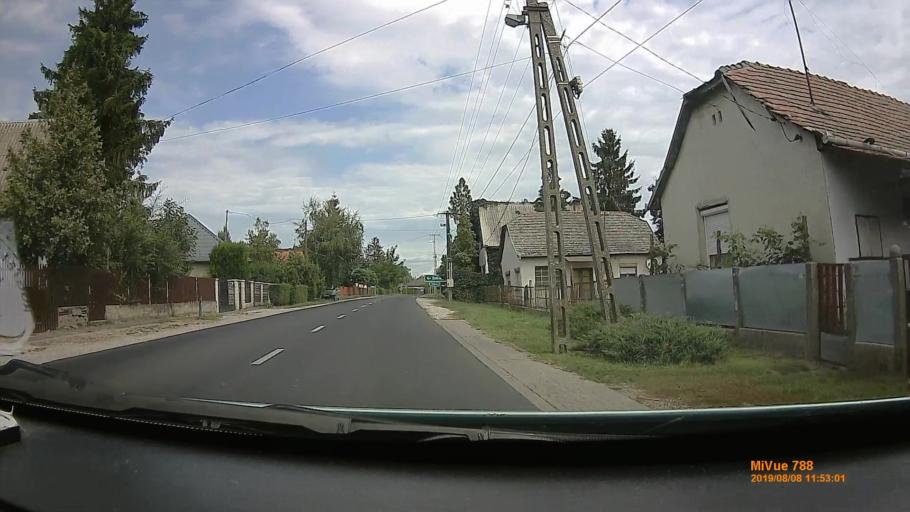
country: HU
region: Szabolcs-Szatmar-Bereg
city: Nyirmihalydi
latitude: 47.7299
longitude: 21.9589
